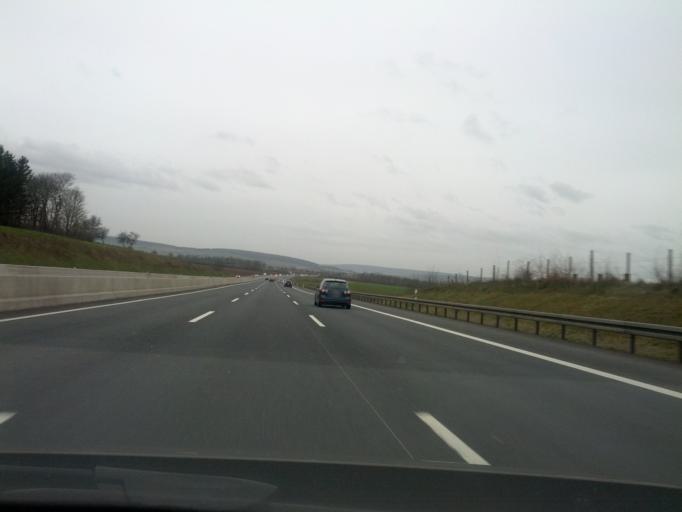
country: DE
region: Lower Saxony
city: Haverlah
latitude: 52.0290
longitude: 10.1718
